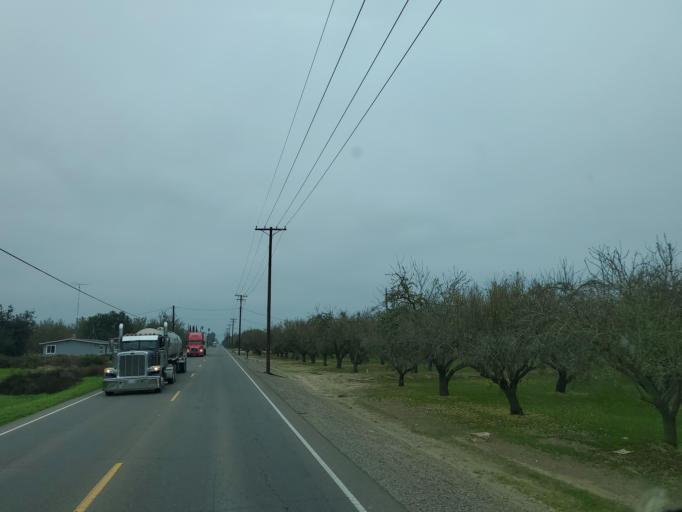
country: US
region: California
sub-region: Stanislaus County
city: Keyes
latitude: 37.5512
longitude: -120.8864
